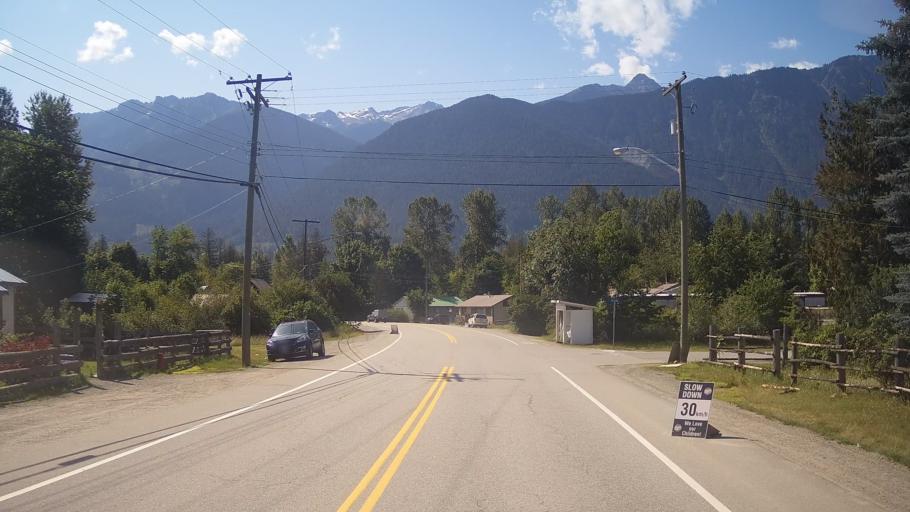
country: CA
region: British Columbia
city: Pemberton
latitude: 50.3187
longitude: -122.7200
